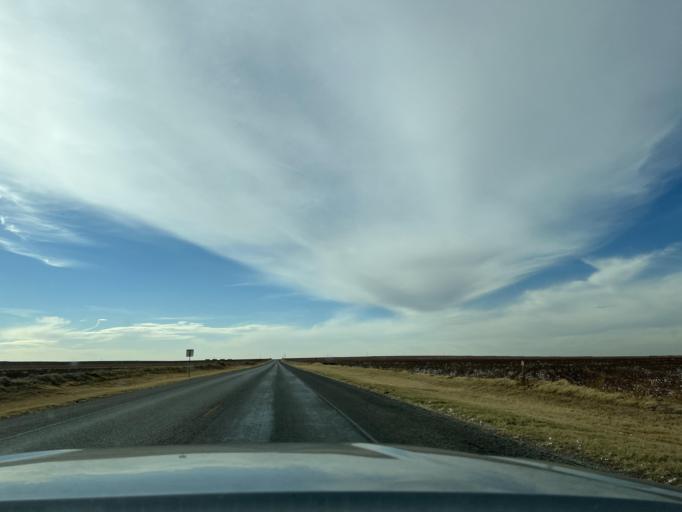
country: US
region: Texas
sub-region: Fisher County
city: Roby
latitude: 32.7419
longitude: -100.4455
